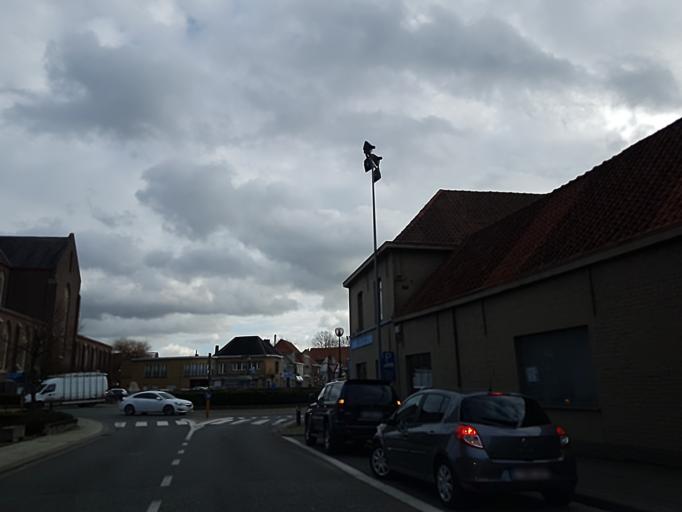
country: BE
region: Flanders
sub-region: Provincie Oost-Vlaanderen
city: Kruishoutem
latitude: 50.9048
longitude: 3.5277
